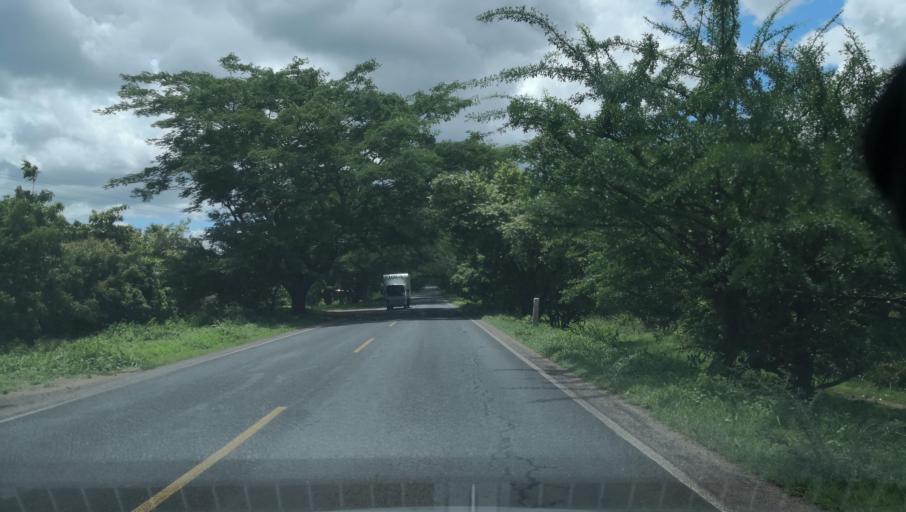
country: NI
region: Madriz
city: Palacaguina
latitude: 13.4257
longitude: -86.4044
